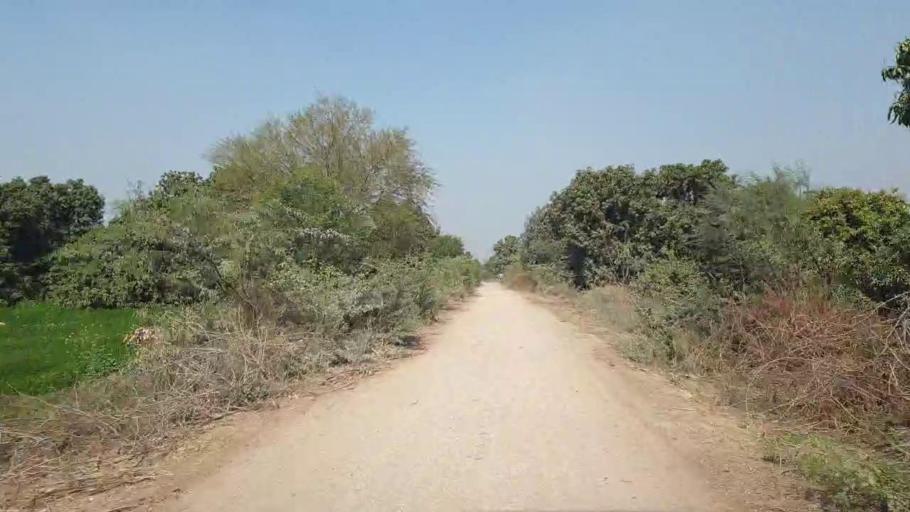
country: PK
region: Sindh
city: Chambar
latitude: 25.4093
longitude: 68.8879
